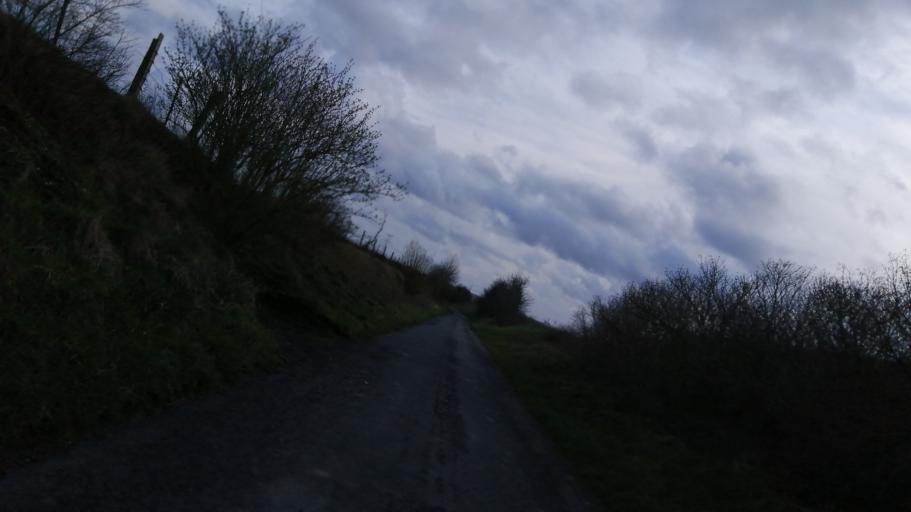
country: FR
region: Nord-Pas-de-Calais
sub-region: Departement du Pas-de-Calais
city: Beaurains
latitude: 50.2536
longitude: 2.7866
